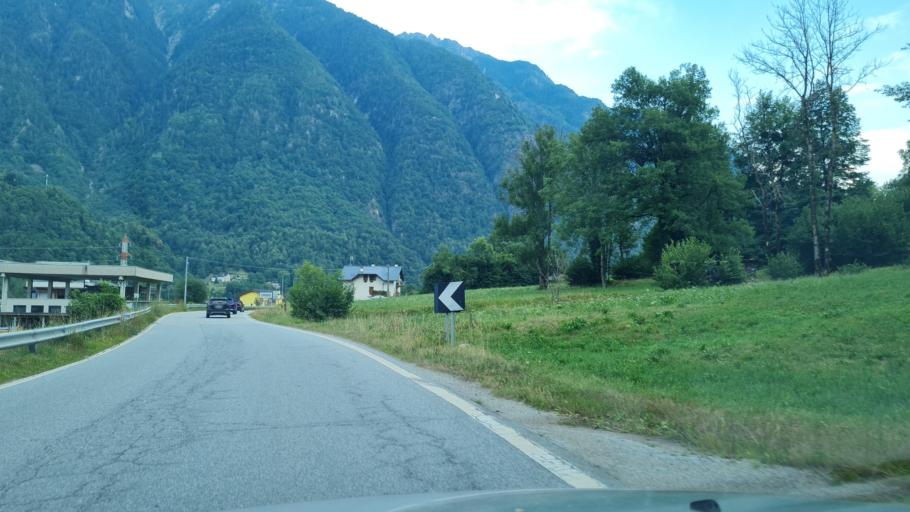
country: IT
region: Piedmont
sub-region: Provincia Verbano-Cusio-Ossola
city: Crodo
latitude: 46.2330
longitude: 8.3215
